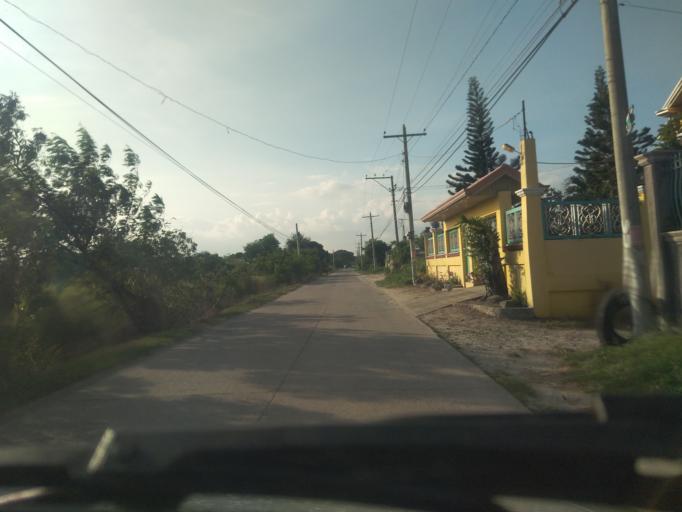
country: PH
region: Central Luzon
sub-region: Province of Pampanga
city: Mexico
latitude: 15.0825
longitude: 120.7011
